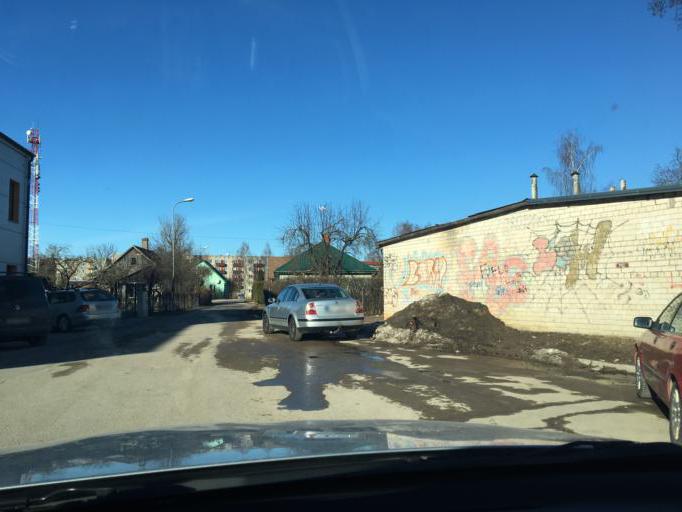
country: LV
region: Jekabpils Rajons
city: Jekabpils
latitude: 56.4905
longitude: 25.8661
